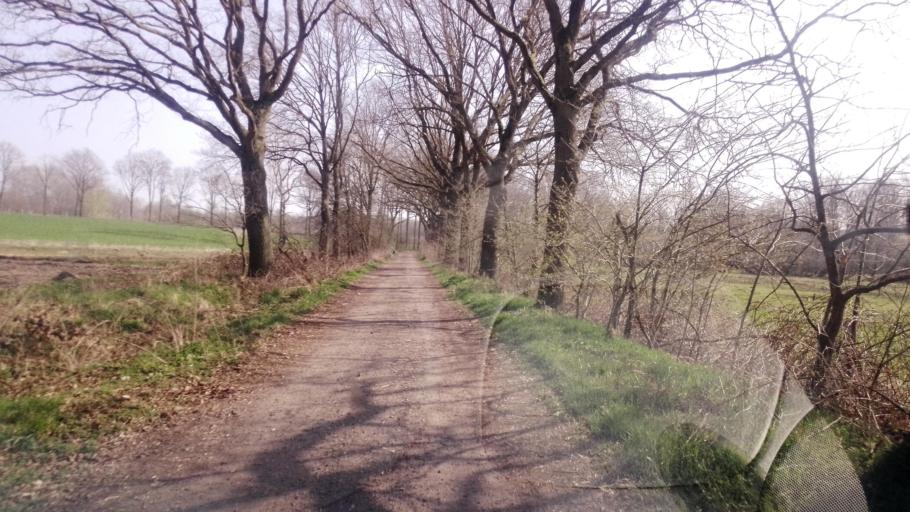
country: NL
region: Limburg
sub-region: Gemeente Peel en Maas
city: Maasbree
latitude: 51.3810
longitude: 6.0272
